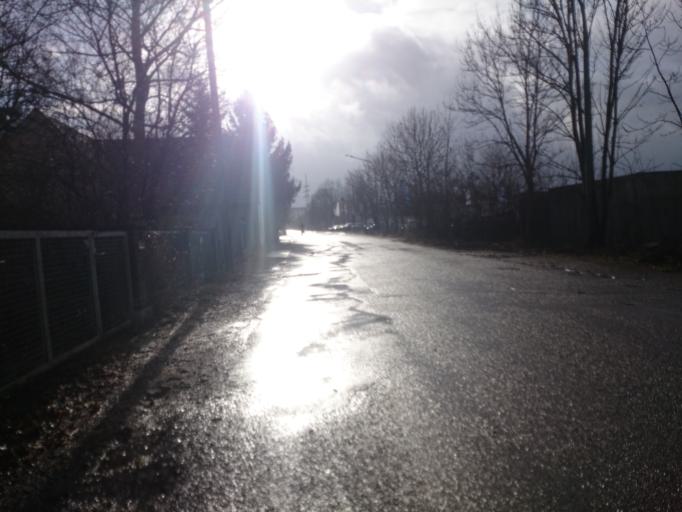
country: DE
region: Bavaria
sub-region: Swabia
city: Konigsbrunn
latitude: 48.2864
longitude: 10.8862
